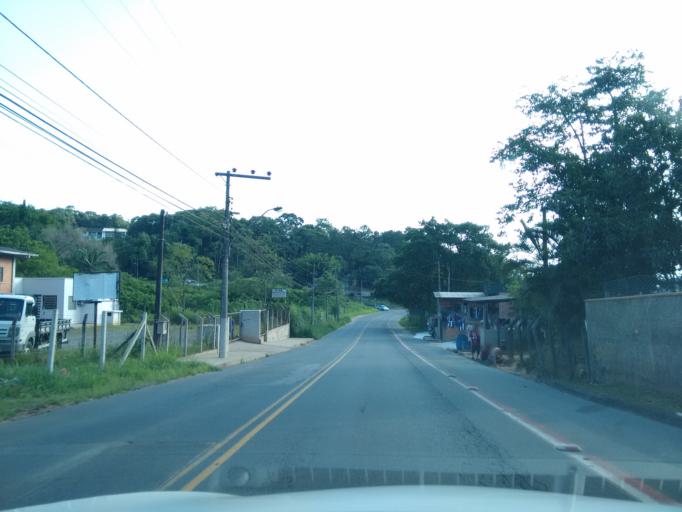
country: BR
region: Santa Catarina
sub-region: Blumenau
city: Blumenau
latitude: -26.8580
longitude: -49.0768
